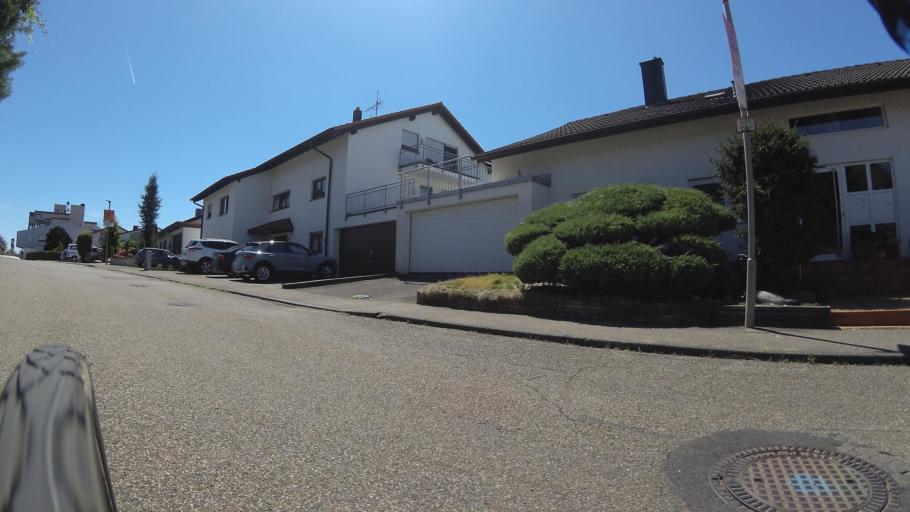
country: DE
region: Baden-Wuerttemberg
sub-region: Regierungsbezirk Stuttgart
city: Leingarten
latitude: 49.1491
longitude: 9.1110
